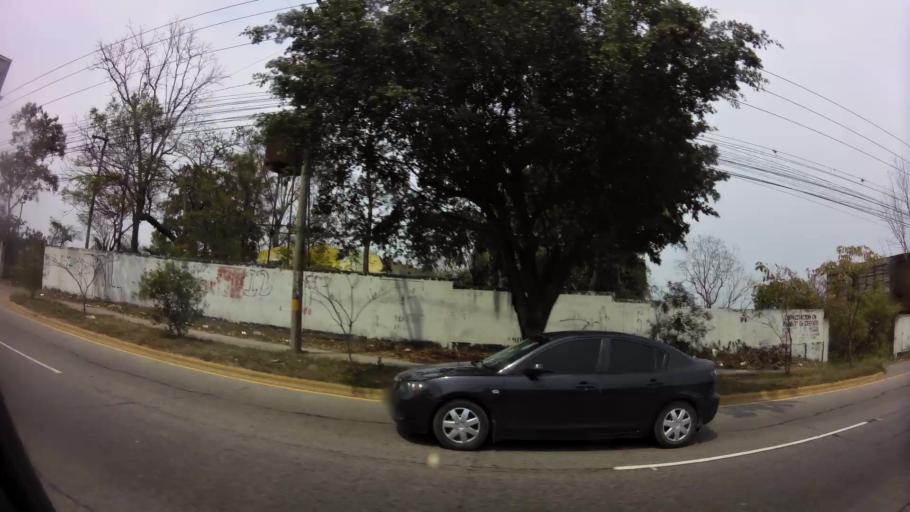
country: HN
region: Cortes
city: San Pedro Sula
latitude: 15.4611
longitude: -88.0295
